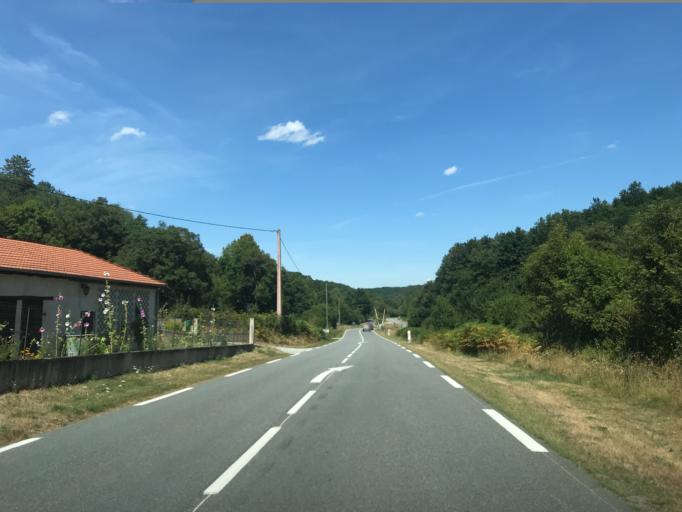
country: FR
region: Limousin
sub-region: Departement de la Creuse
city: Felletin
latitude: 45.9033
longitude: 2.1869
